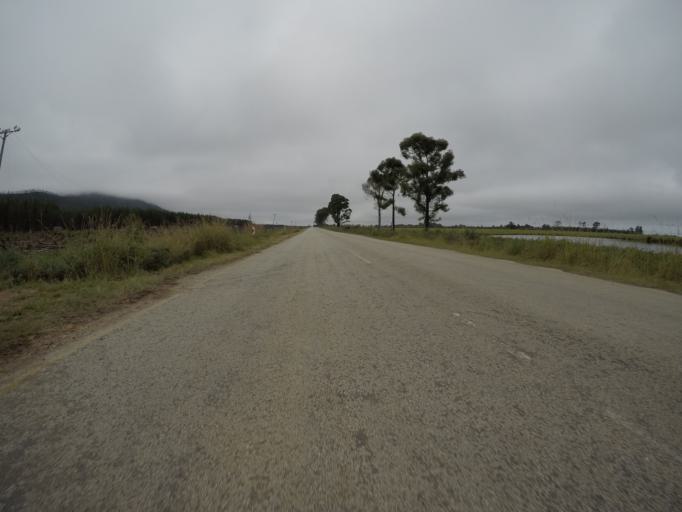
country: ZA
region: Eastern Cape
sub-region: Cacadu District Municipality
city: Kareedouw
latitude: -33.9832
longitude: 24.0568
